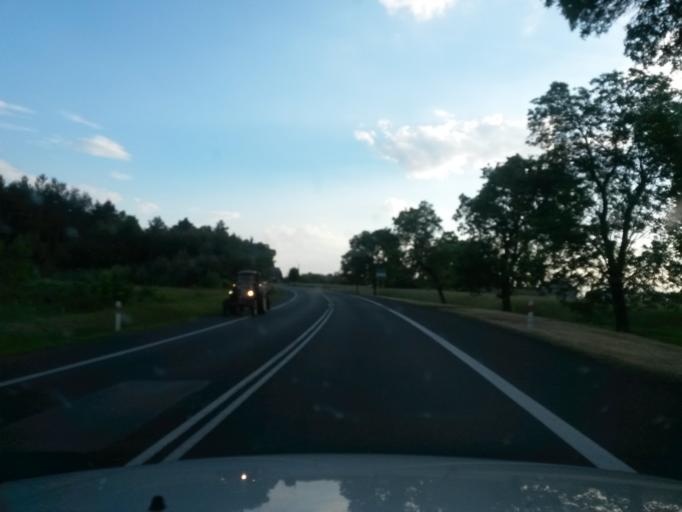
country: PL
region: Lodz Voivodeship
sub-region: Powiat wielunski
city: Osjakow
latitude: 51.3054
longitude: 18.8638
